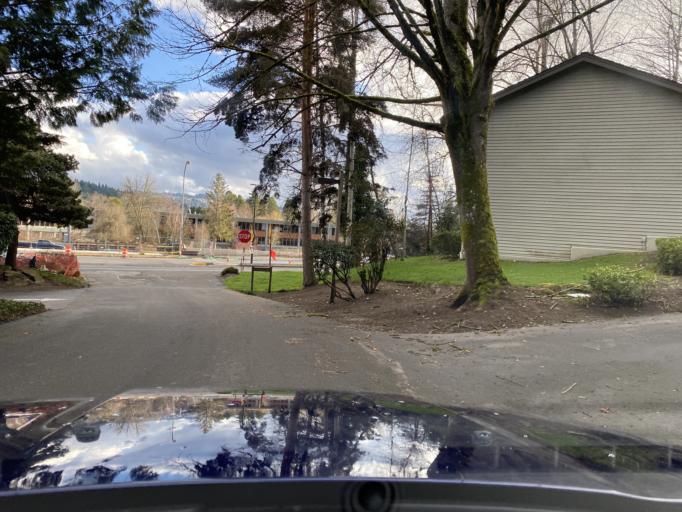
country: US
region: Washington
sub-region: King County
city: Bellevue
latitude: 47.5979
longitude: -122.1937
